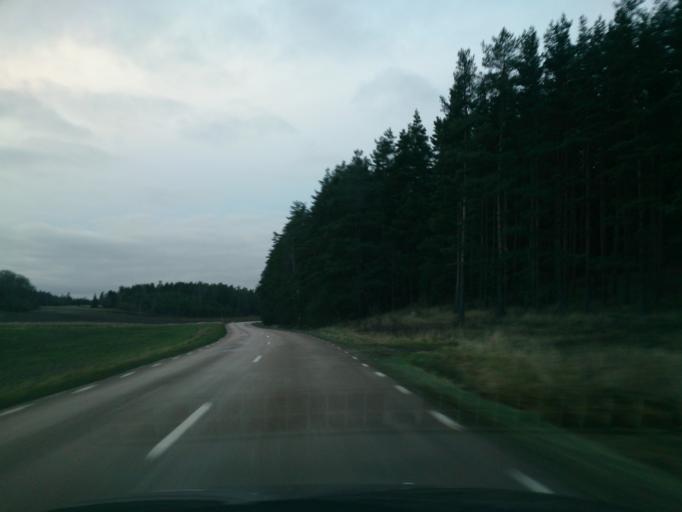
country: SE
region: OEstergoetland
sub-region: Linkopings Kommun
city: Linghem
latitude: 58.4342
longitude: 15.8960
